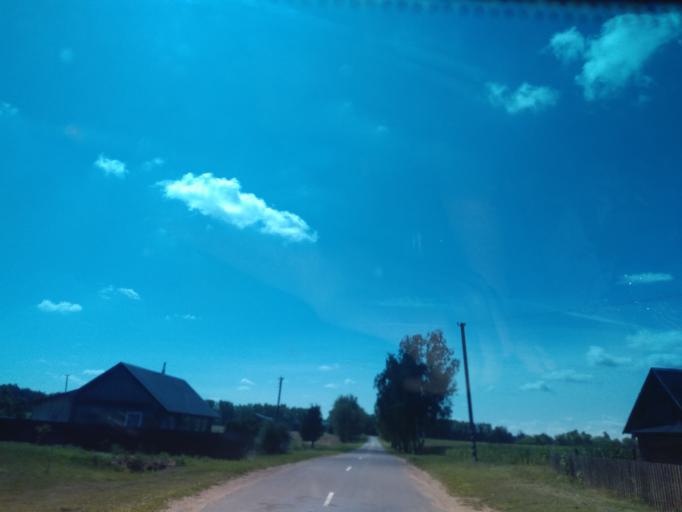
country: BY
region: Minsk
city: Kapyl'
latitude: 53.2509
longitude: 27.1836
